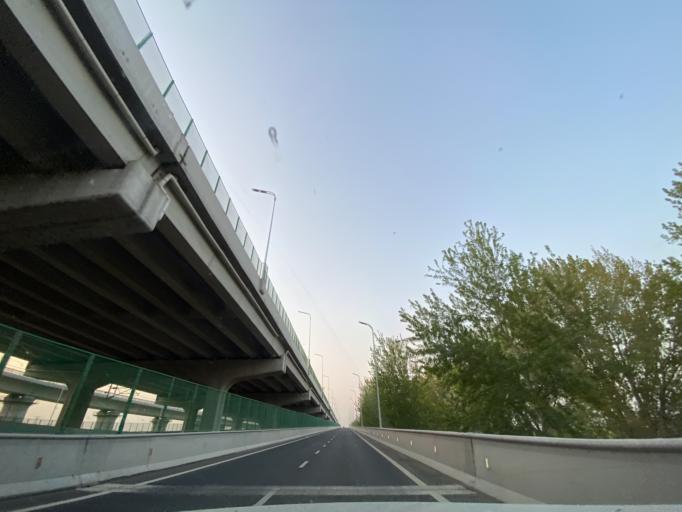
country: CN
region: Beijing
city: Weishanzhuang
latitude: 39.6187
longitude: 116.3789
